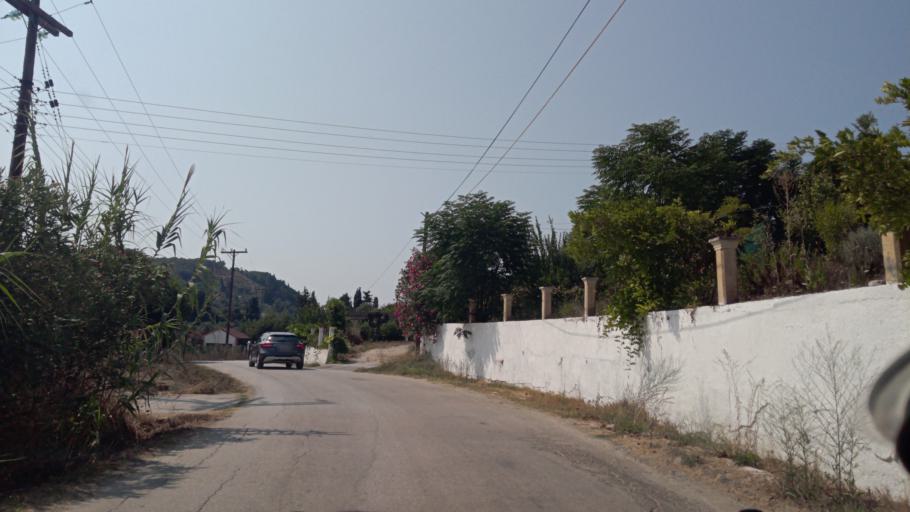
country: GR
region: Ionian Islands
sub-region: Nomos Kerkyras
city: Perivoli
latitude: 39.4038
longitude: 20.0268
